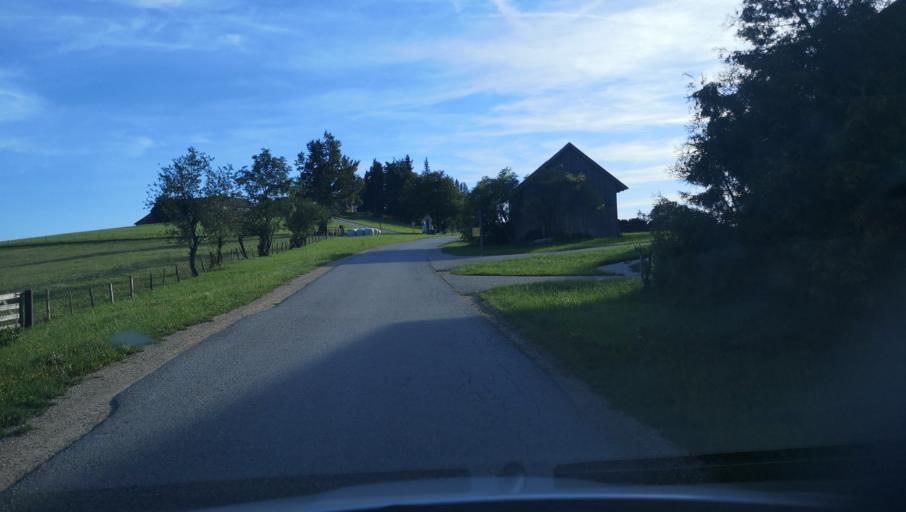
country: AT
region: Lower Austria
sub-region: Politischer Bezirk Amstetten
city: Euratsfeld
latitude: 48.0270
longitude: 14.9157
